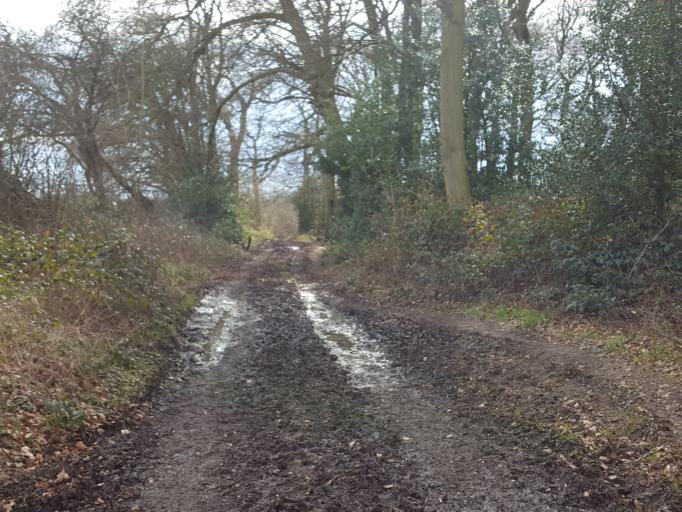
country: GB
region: England
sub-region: Buckinghamshire
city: High Wycombe
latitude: 51.6565
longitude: -0.8138
